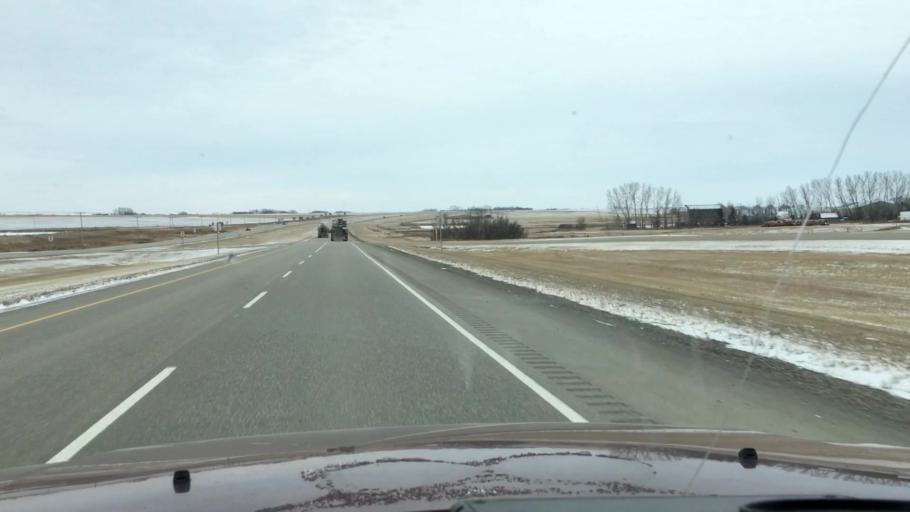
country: CA
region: Saskatchewan
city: Watrous
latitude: 51.2425
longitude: -105.9665
